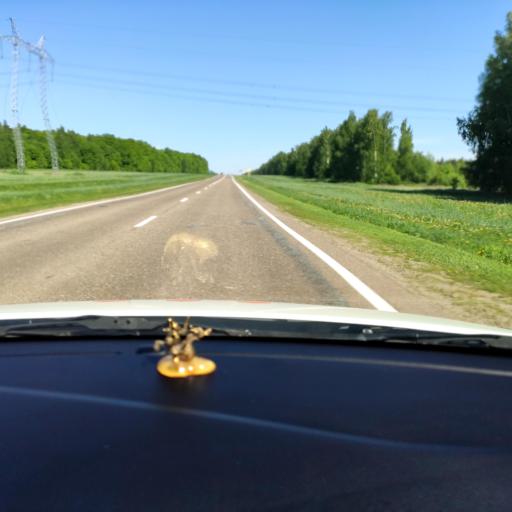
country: RU
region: Tatarstan
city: Vysokaya Gora
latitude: 56.0766
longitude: 49.1889
